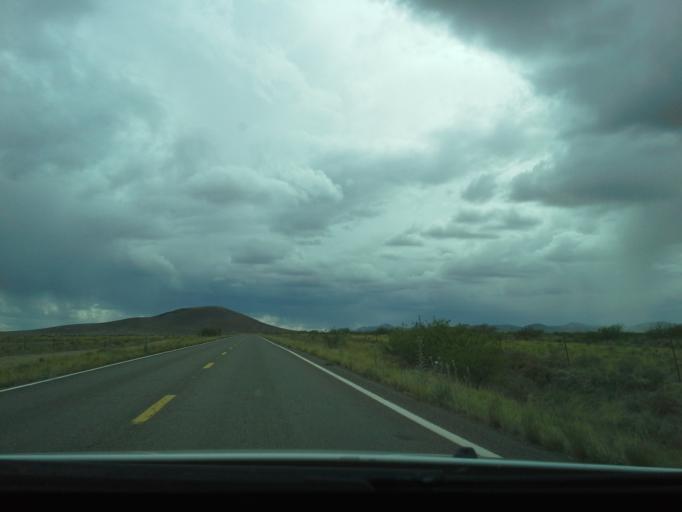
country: US
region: Arizona
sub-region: Cochise County
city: Douglas
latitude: 31.6461
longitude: -109.1686
